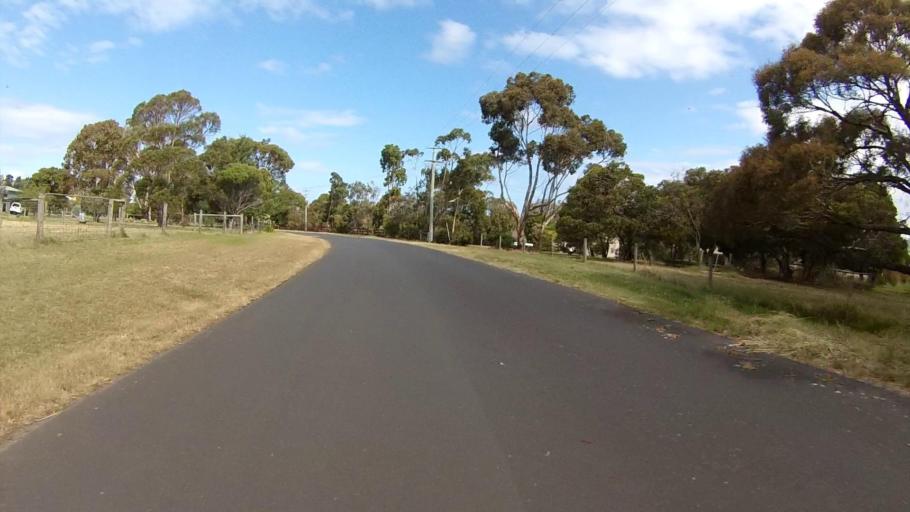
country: AU
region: Tasmania
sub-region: Clarence
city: Acton Park
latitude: -42.8843
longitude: 147.4915
